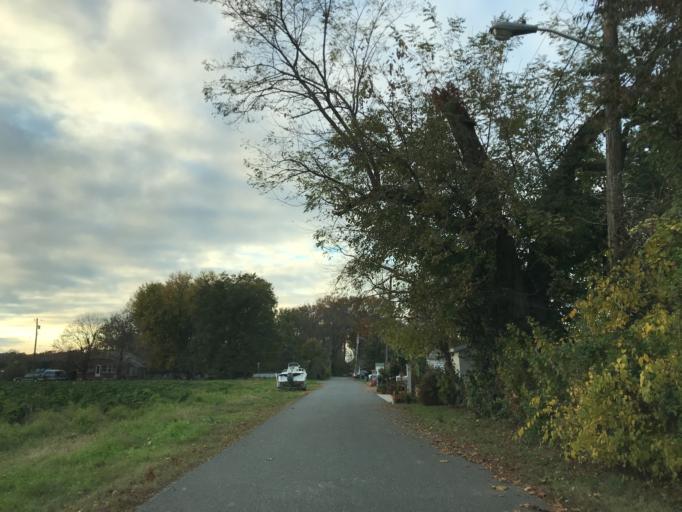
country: US
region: Maryland
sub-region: Baltimore County
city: Bowleys Quarters
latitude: 39.3736
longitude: -76.3750
